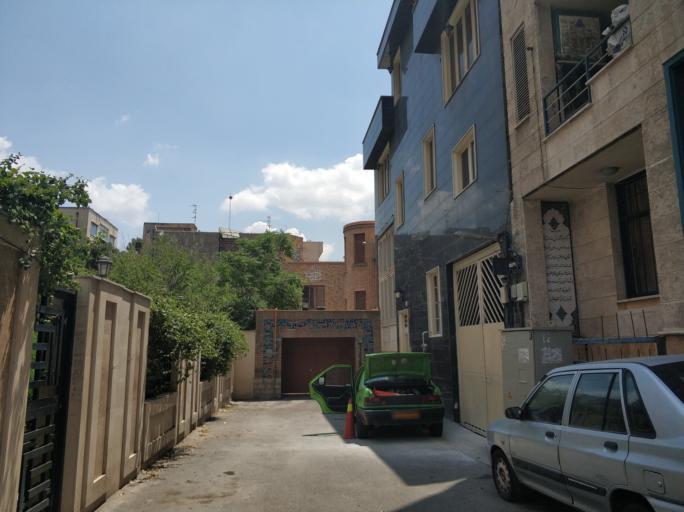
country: IR
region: Tehran
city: Tehran
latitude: 35.7042
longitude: 51.4322
